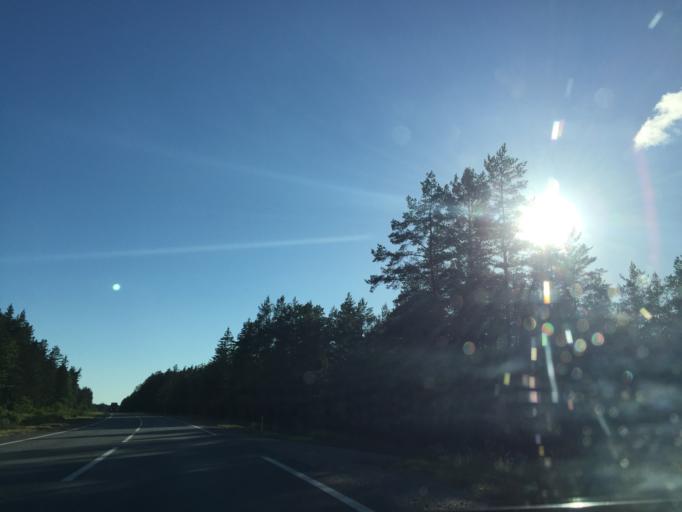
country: LV
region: Ventspils Rajons
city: Piltene
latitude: 57.3944
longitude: 21.8205
